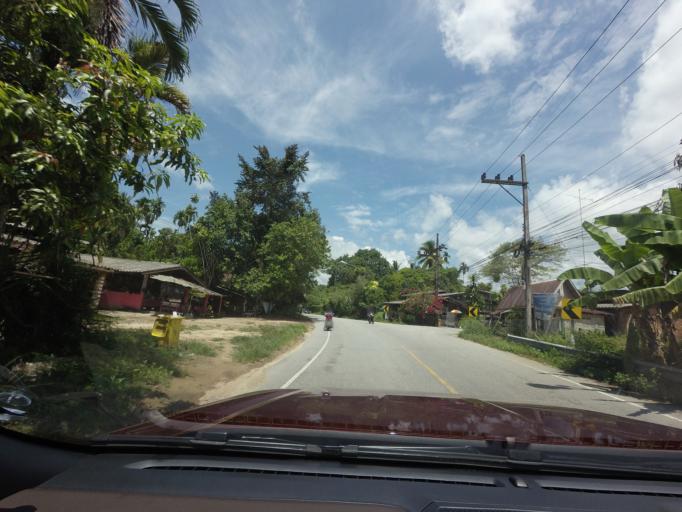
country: TH
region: Narathiwat
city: Ra-ngae
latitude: 6.2520
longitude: 101.6849
